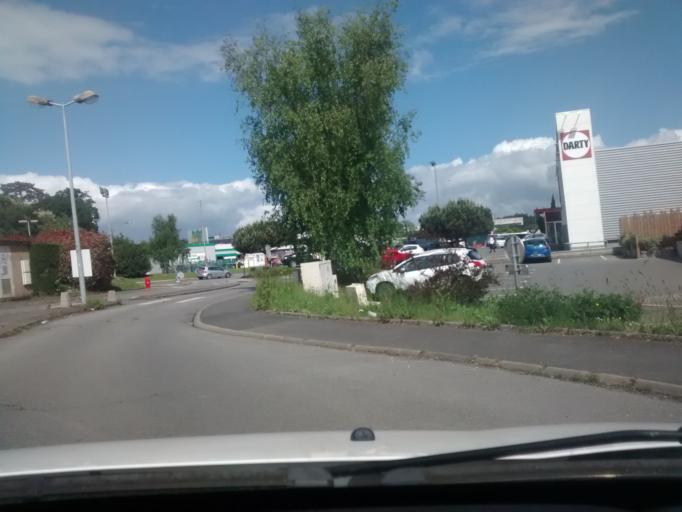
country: FR
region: Brittany
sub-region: Departement d'Ille-et-Vilaine
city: Saint-Gregoire
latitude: 48.1346
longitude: -1.6923
